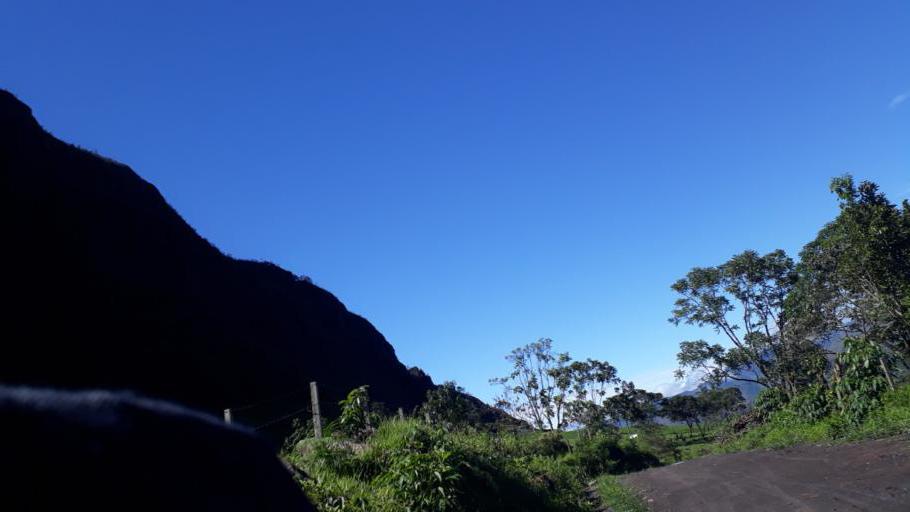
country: CO
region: Casanare
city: Nunchia
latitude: 5.6664
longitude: -72.4227
